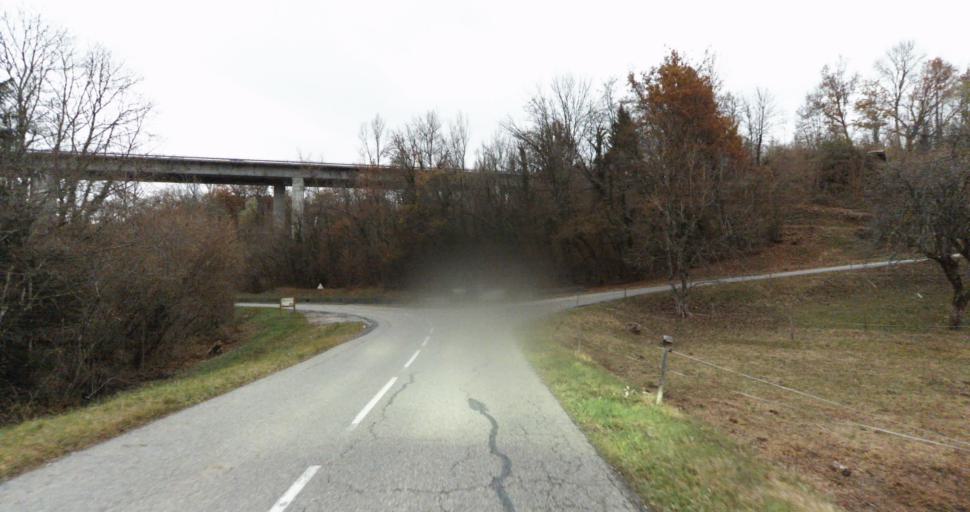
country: FR
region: Rhone-Alpes
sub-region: Departement de la Haute-Savoie
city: Alby-sur-Cheran
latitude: 45.8239
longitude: 6.0304
